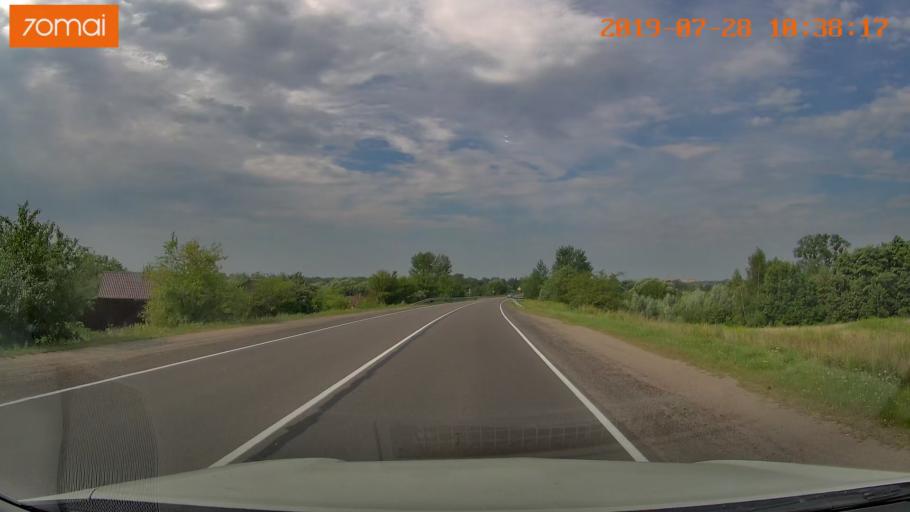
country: RU
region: Kaliningrad
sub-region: Gorod Kaliningrad
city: Kaliningrad
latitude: 54.7251
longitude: 20.4013
